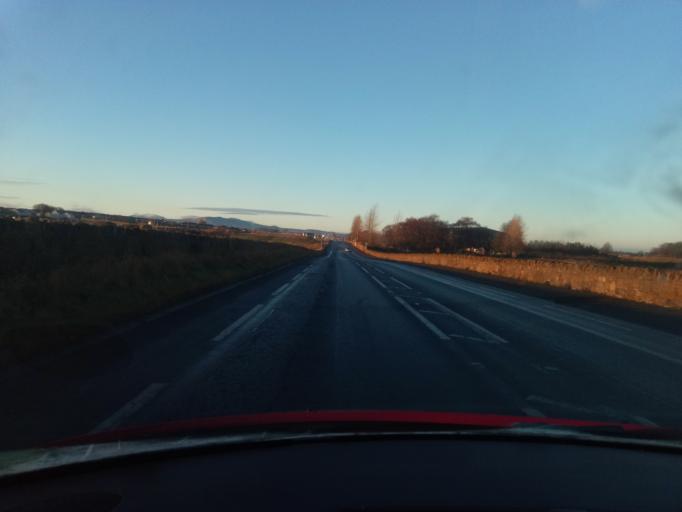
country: GB
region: Scotland
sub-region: East Lothian
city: Prestonpans
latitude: 55.9442
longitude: -2.9951
